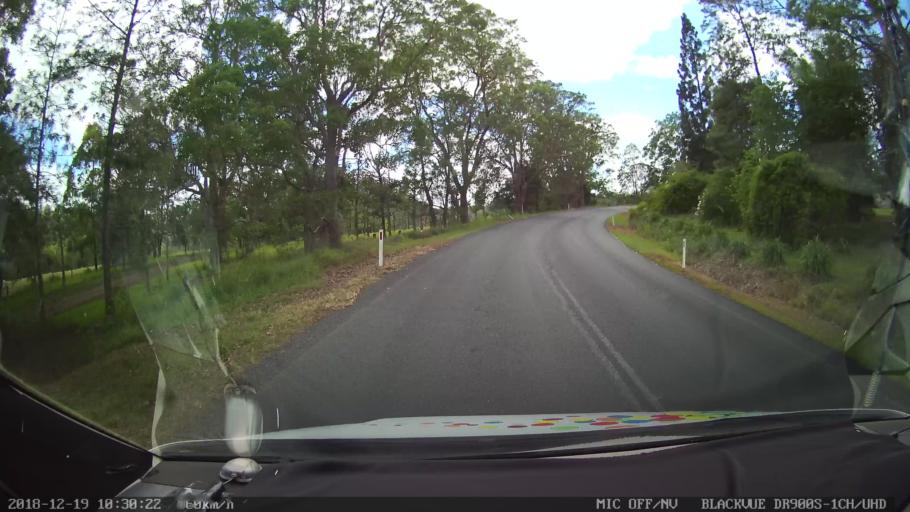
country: AU
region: New South Wales
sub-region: Lismore Municipality
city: Larnook
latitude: -28.5892
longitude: 153.1066
